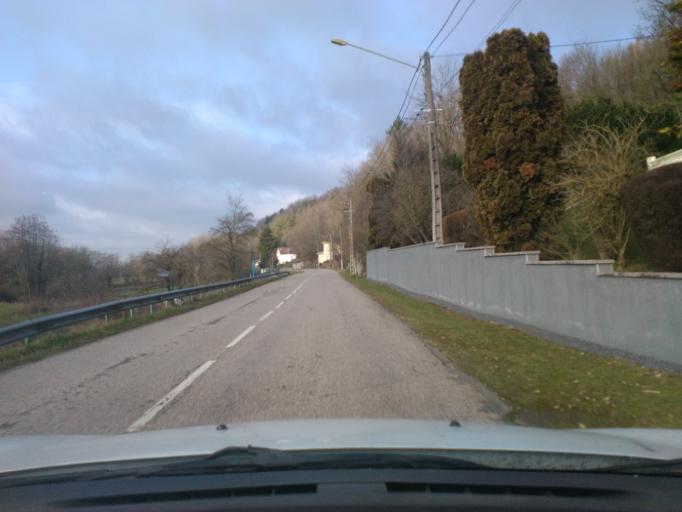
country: FR
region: Lorraine
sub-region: Departement des Vosges
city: Chatel-sur-Moselle
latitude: 48.3025
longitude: 6.4114
